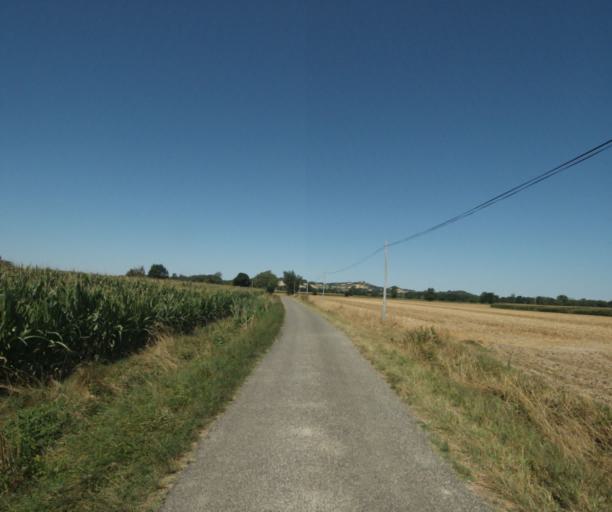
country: FR
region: Midi-Pyrenees
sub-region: Departement de la Haute-Garonne
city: Revel
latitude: 43.4861
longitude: 1.9649
